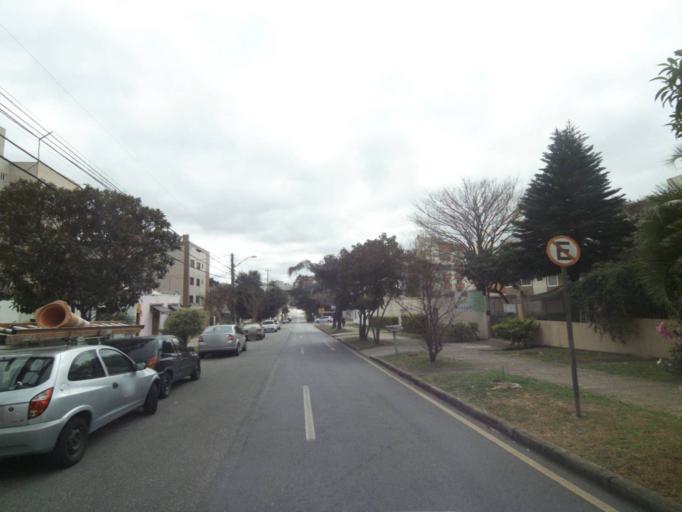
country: BR
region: Parana
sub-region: Curitiba
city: Curitiba
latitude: -25.4600
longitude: -49.2925
